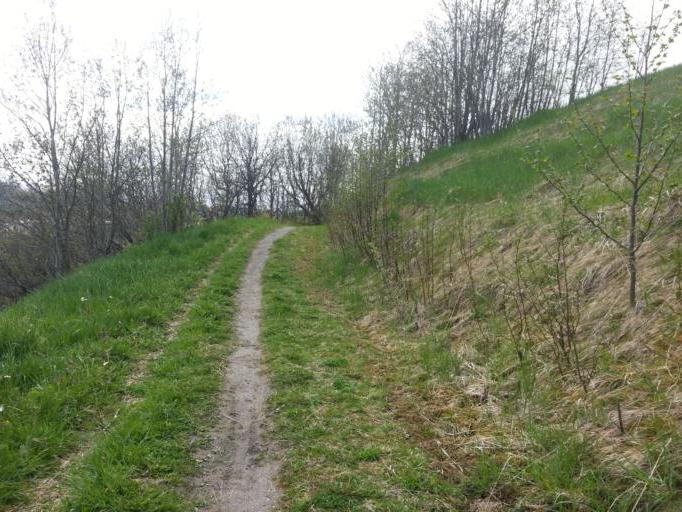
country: NO
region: Sor-Trondelag
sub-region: Trondheim
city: Trondheim
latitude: 63.3872
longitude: 10.3668
